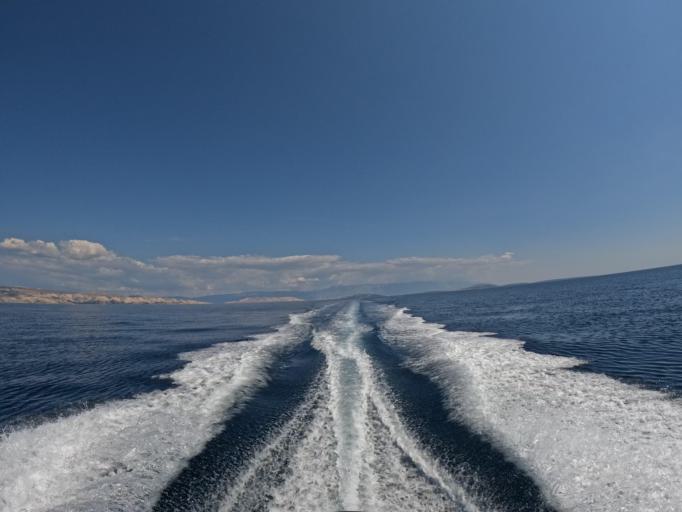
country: HR
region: Primorsko-Goranska
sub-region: Grad Krk
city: Krk
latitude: 44.9201
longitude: 14.5656
